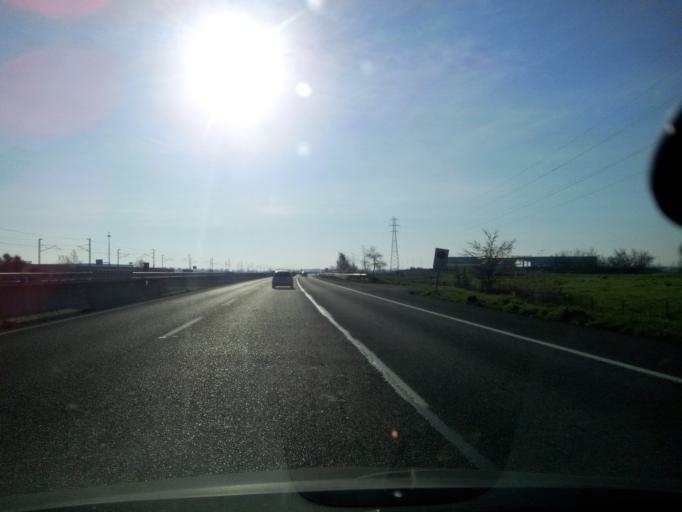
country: IT
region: Emilia-Romagna
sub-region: Provincia di Reggio Emilia
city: Prato
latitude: 44.7098
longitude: 10.7221
